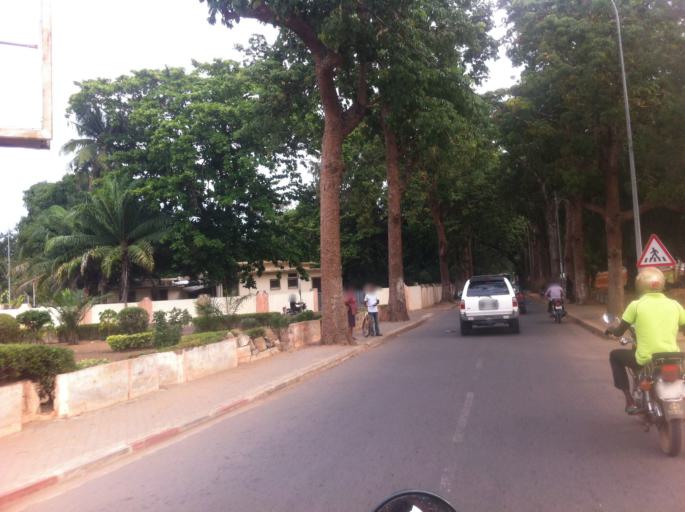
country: TG
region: Maritime
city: Lome
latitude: 6.1319
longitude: 1.2178
